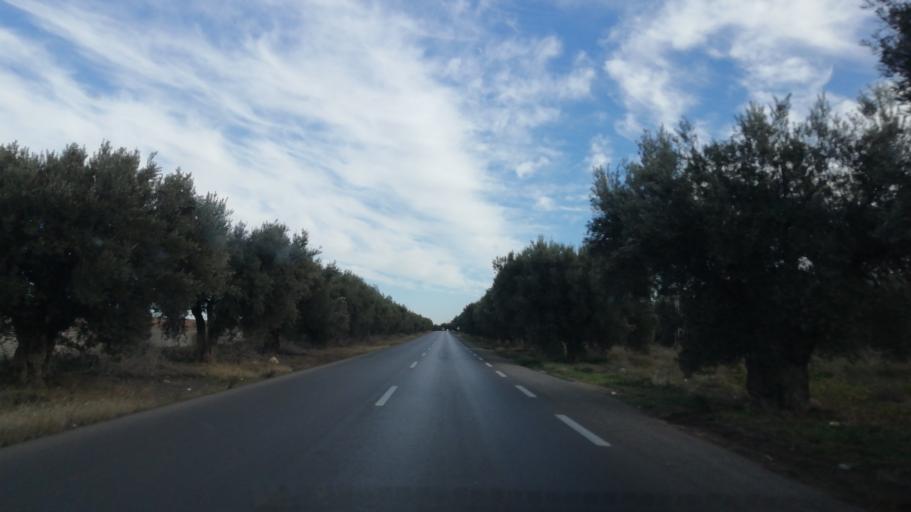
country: DZ
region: Sidi Bel Abbes
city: Sidi Bel Abbes
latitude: 35.1783
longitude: -0.4416
